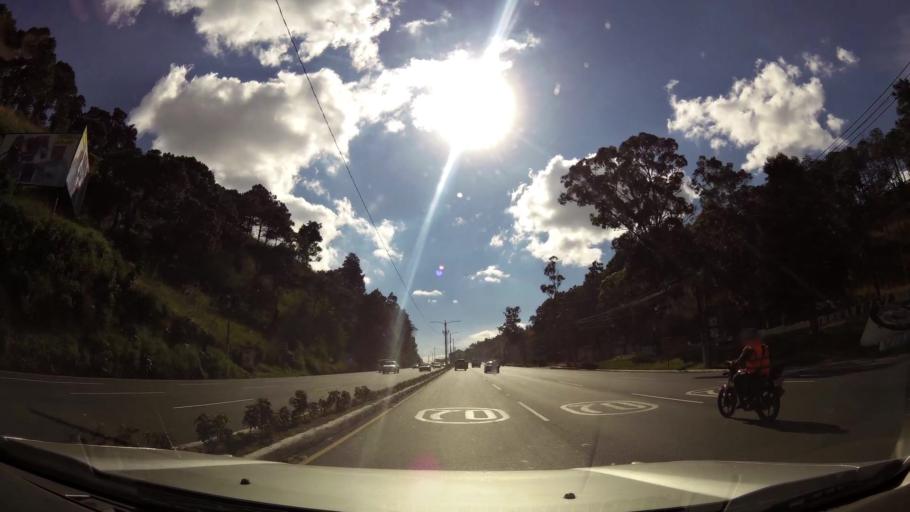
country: GT
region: Guatemala
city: Villa Nueva
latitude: 14.5448
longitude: -90.5820
